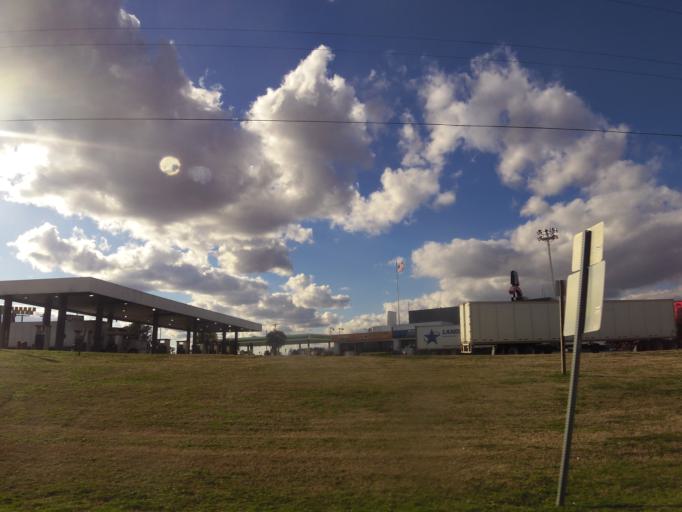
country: US
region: South Carolina
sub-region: Clarendon County
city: Manning
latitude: 33.7043
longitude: -80.2409
